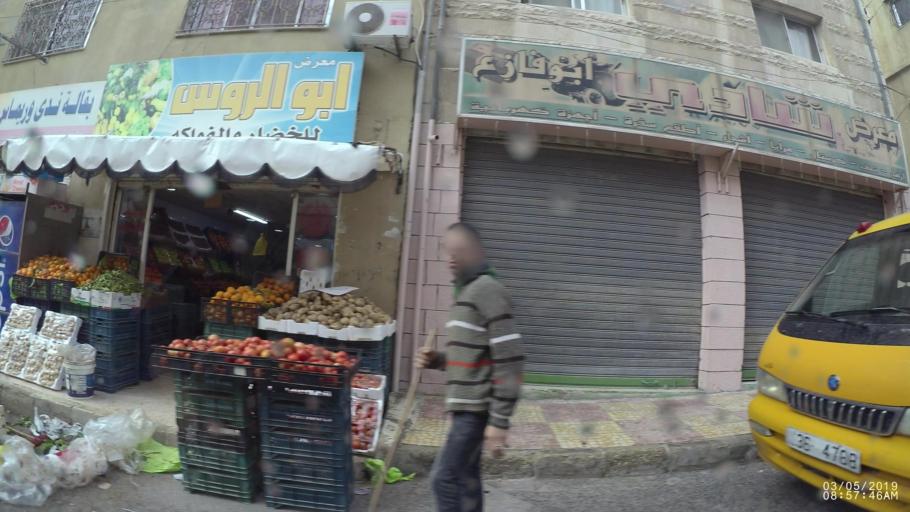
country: JO
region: Amman
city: Amman
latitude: 31.9582
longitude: 35.9386
